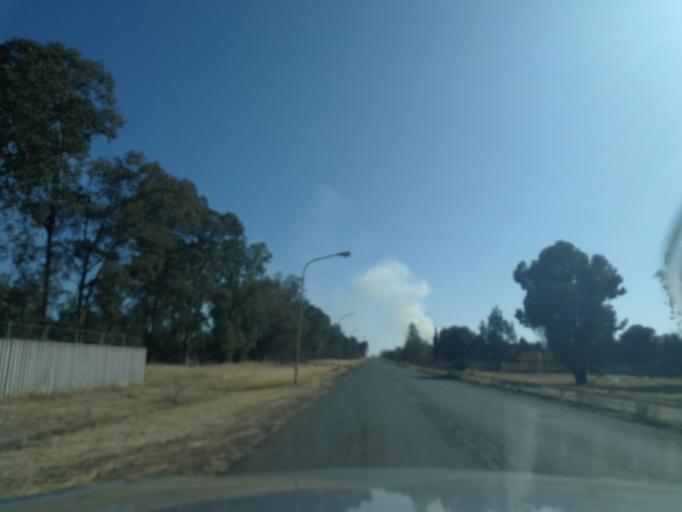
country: ZA
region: Orange Free State
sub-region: Fezile Dabi District Municipality
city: Kroonstad
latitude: -27.6375
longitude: 27.2192
